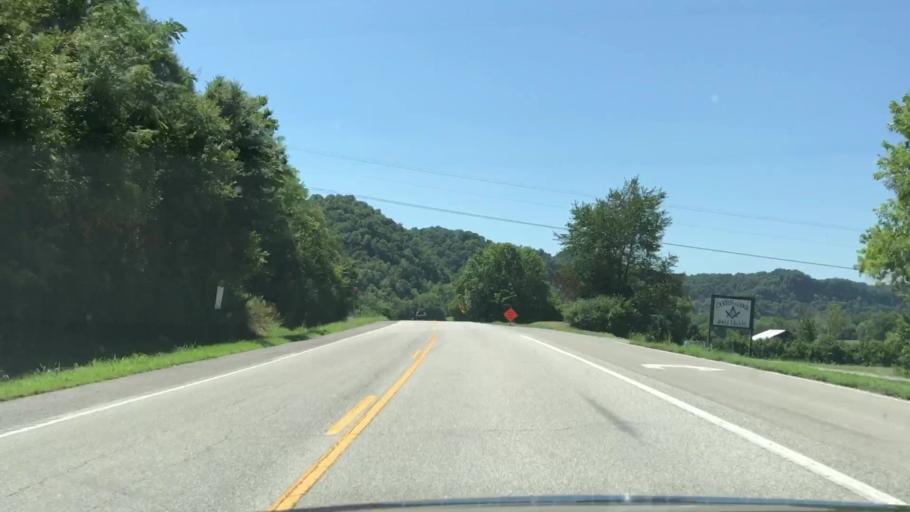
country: US
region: Tennessee
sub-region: Clay County
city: Celina
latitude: 36.5187
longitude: -85.5347
